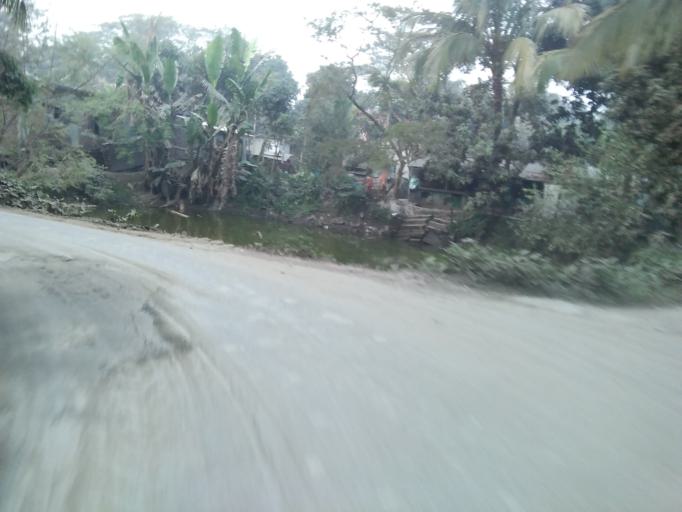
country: IN
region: West Bengal
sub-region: North 24 Parganas
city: Taki
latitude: 22.6513
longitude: 88.9972
